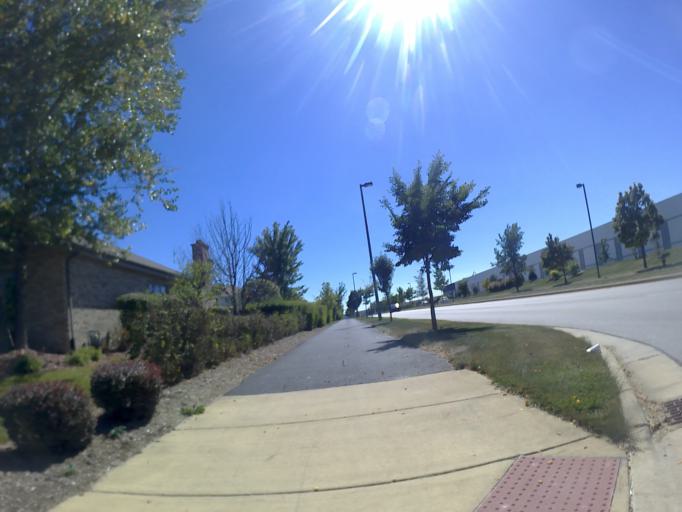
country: US
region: Illinois
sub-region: DuPage County
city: Woodridge
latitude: 41.7172
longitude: -88.0269
